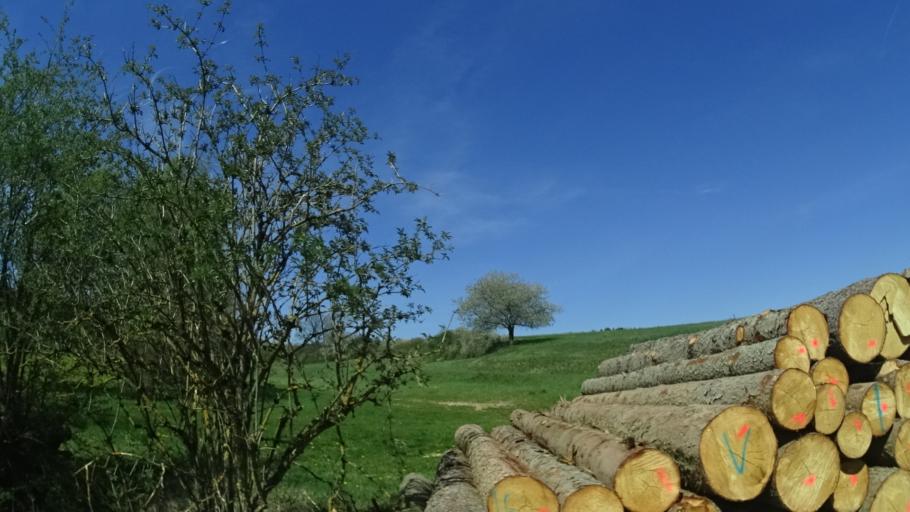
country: DE
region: Bavaria
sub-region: Upper Franconia
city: Weitramsdorf
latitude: 50.2871
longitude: 10.7852
